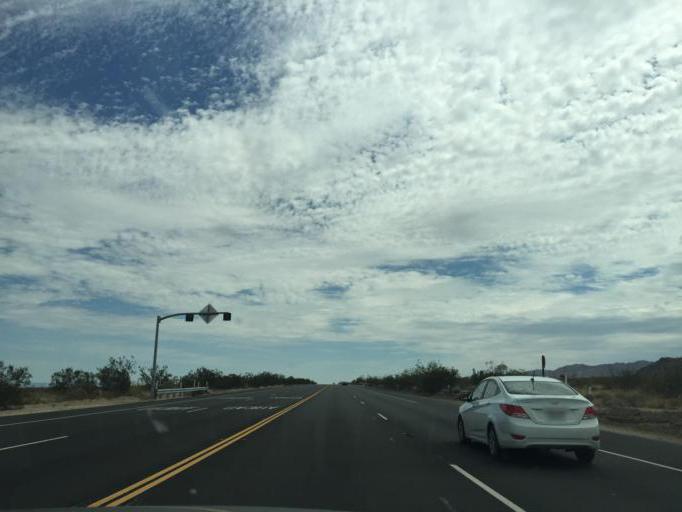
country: US
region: California
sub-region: San Bernardino County
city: Joshua Tree
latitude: 34.1351
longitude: -116.2106
